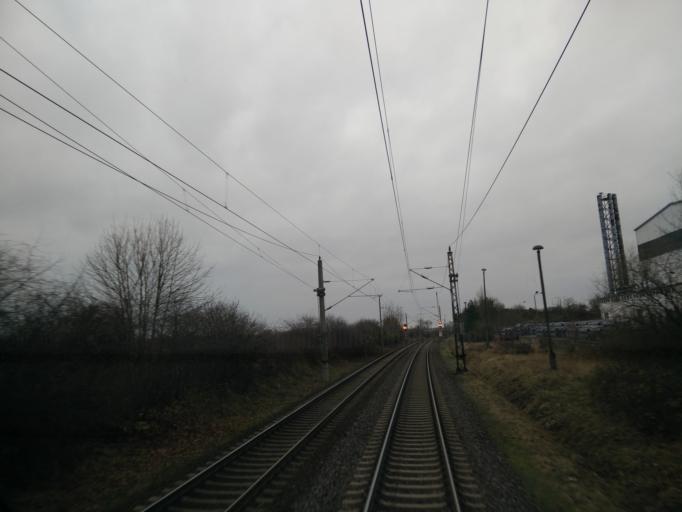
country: DE
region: Mecklenburg-Vorpommern
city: Lewenberg
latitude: 53.6514
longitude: 11.4013
